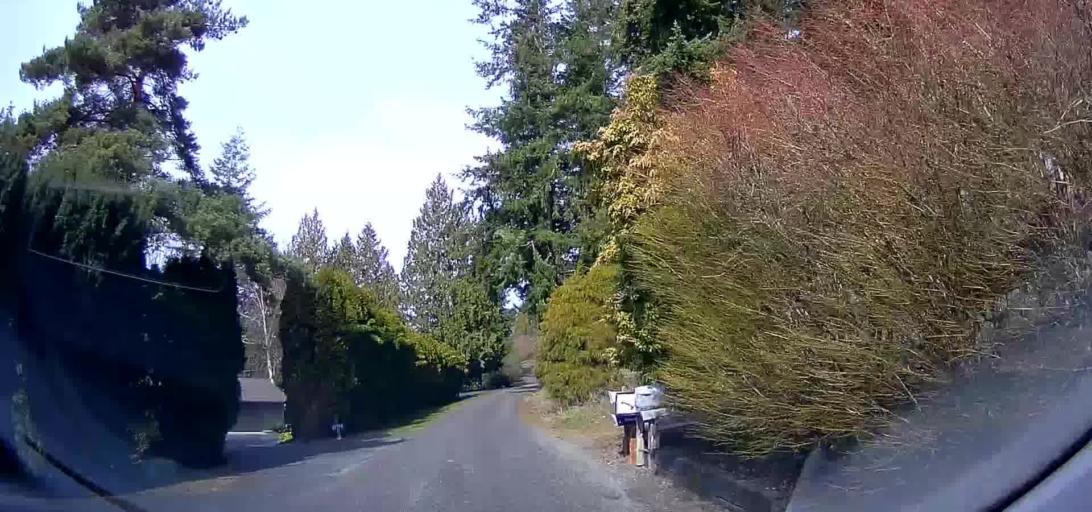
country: US
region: Washington
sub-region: Skagit County
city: Mount Vernon
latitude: 48.3952
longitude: -122.3150
